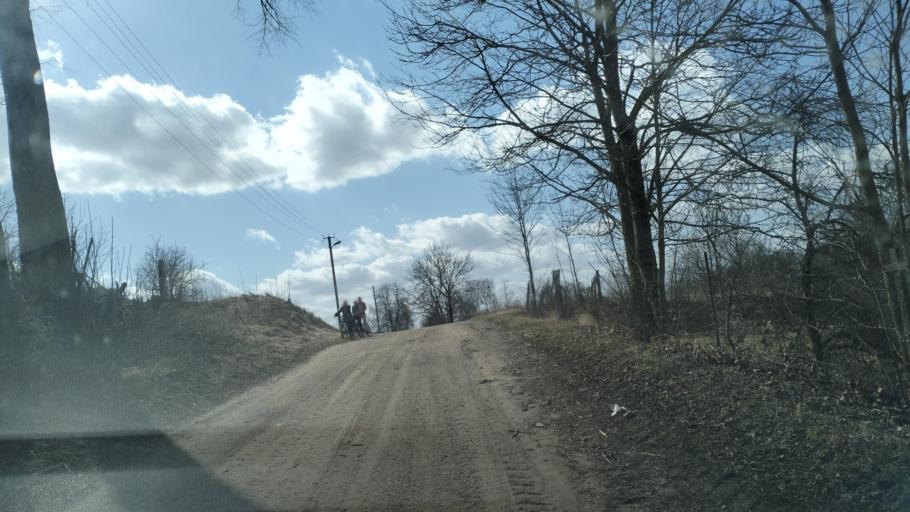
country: BY
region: Grodnenskaya
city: Karelichy
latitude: 53.6542
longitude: 26.0979
